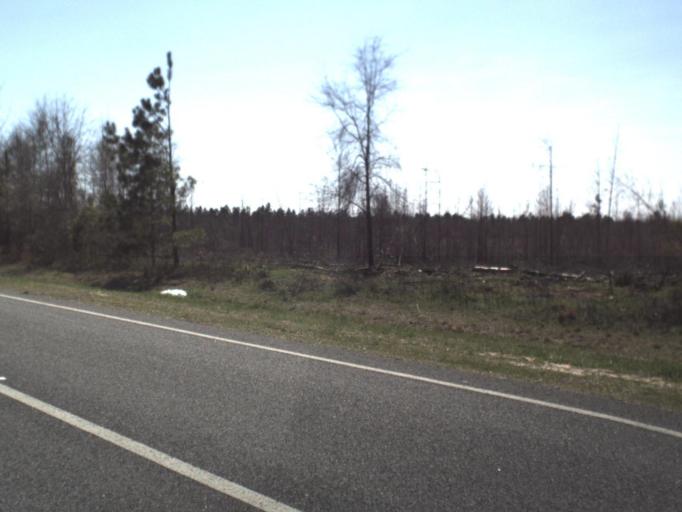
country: US
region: Florida
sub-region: Jackson County
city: Graceville
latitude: 30.8871
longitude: -85.3676
